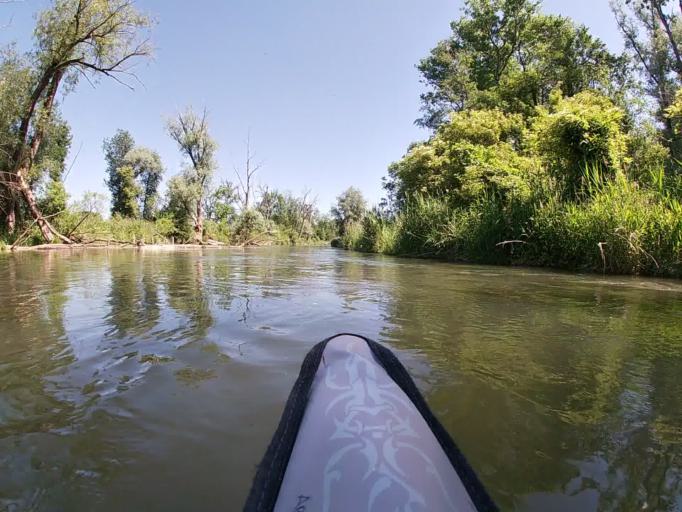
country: DE
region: Bavaria
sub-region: Upper Bavaria
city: Rosenheim
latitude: 47.8845
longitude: 12.1342
